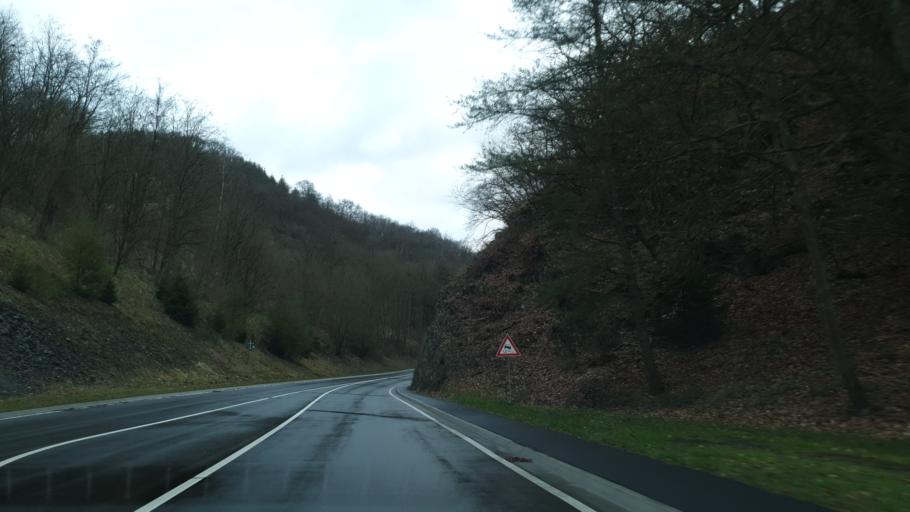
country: DE
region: Rheinland-Pfalz
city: Laurenburg
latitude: 50.3302
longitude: 7.9026
